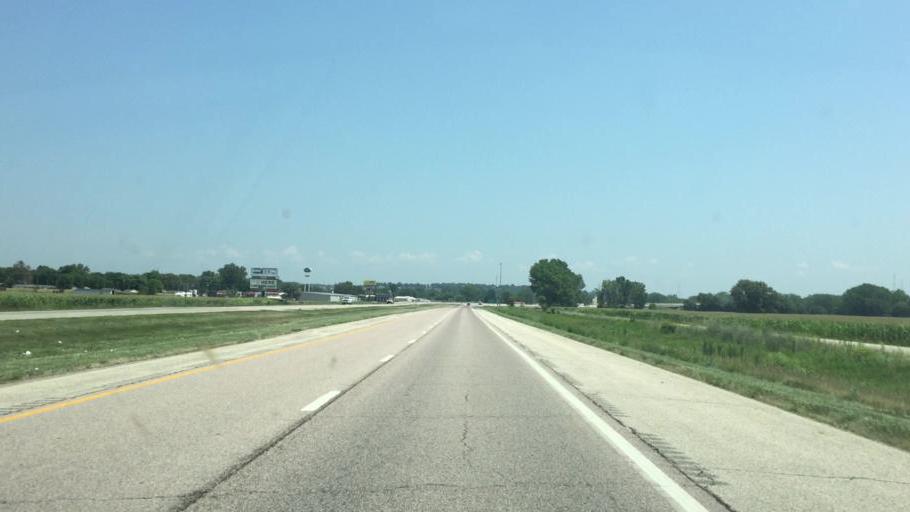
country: US
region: Kansas
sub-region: Doniphan County
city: Elwood
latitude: 39.7458
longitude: -94.8783
